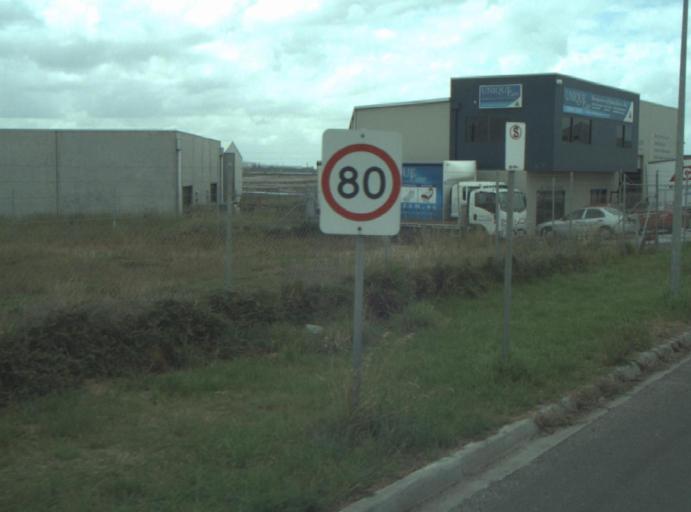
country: AU
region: Victoria
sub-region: Greater Geelong
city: Leopold
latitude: -38.1664
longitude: 144.4232
